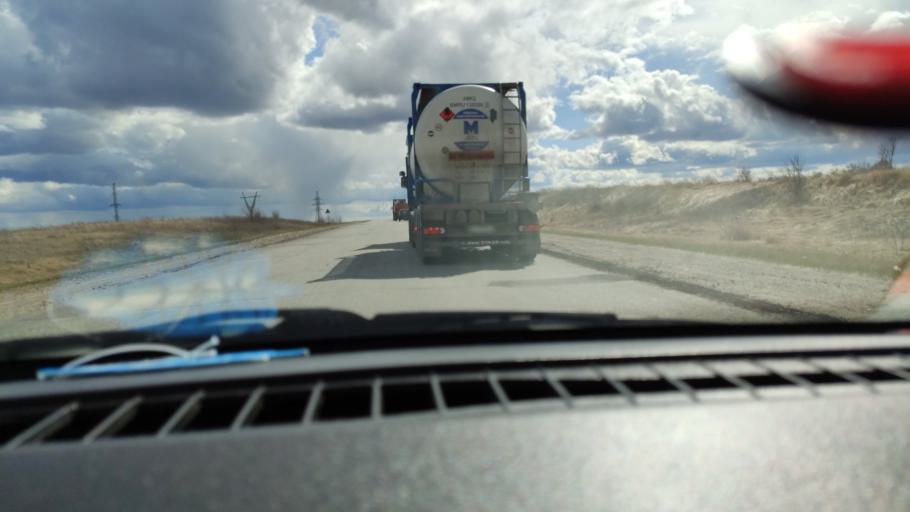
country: RU
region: Samara
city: Varlamovo
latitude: 53.0841
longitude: 48.3546
